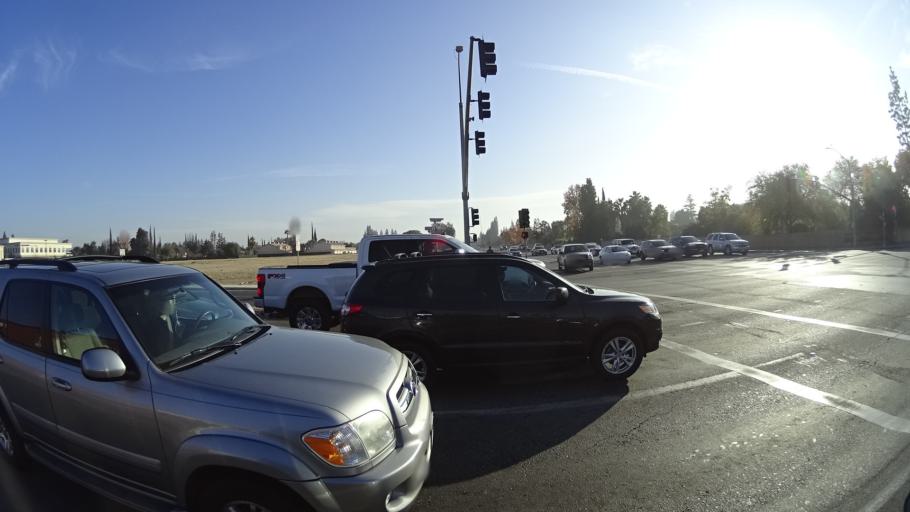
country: US
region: California
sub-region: Kern County
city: Greenacres
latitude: 35.3546
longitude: -119.0924
